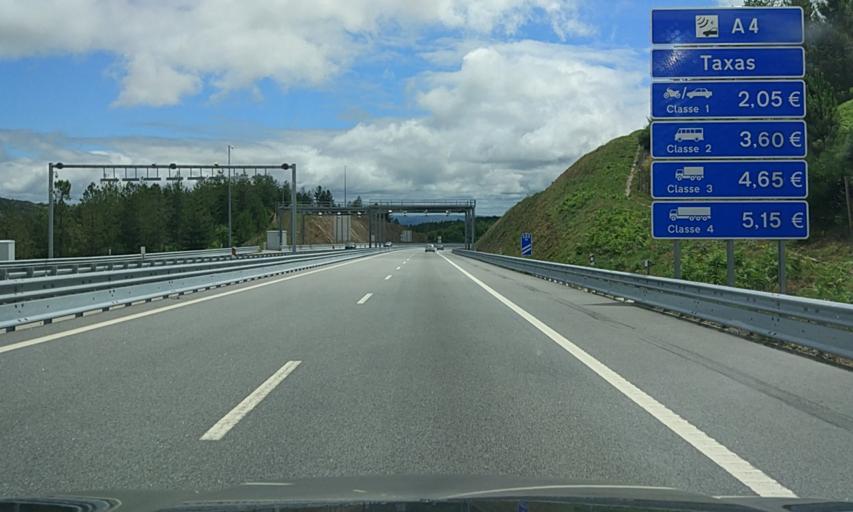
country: PT
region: Vila Real
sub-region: Santa Marta de Penaguiao
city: Santa Marta de Penaguiao
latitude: 41.2781
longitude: -7.8427
